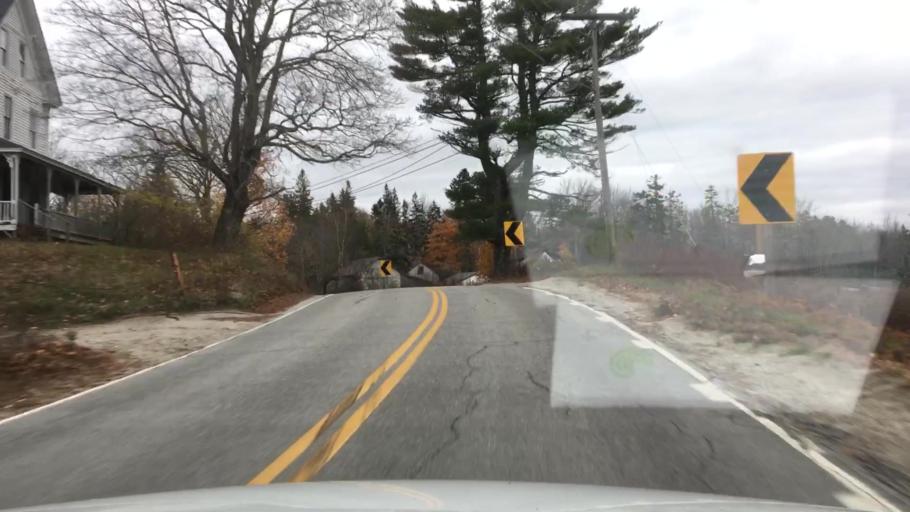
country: US
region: Maine
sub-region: Hancock County
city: Sedgwick
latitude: 44.3546
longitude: -68.5490
